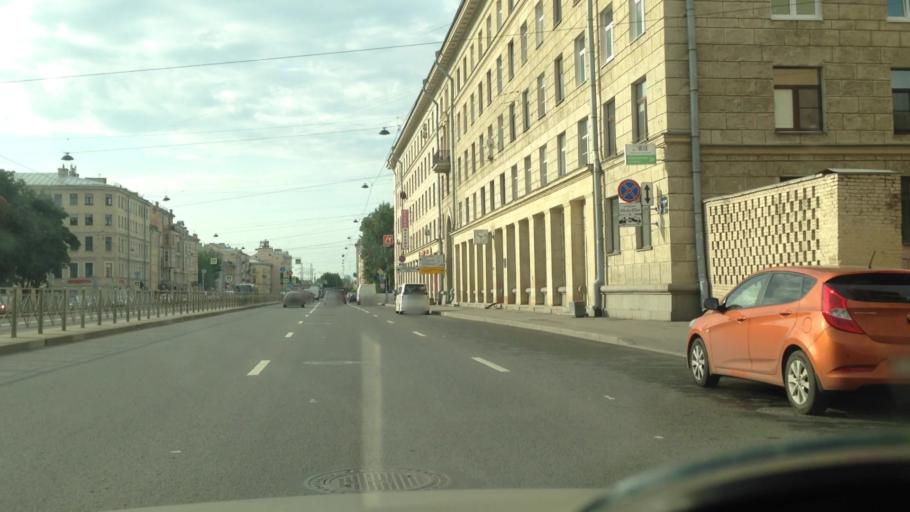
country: RU
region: St.-Petersburg
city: Centralniy
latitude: 59.9110
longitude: 30.3477
